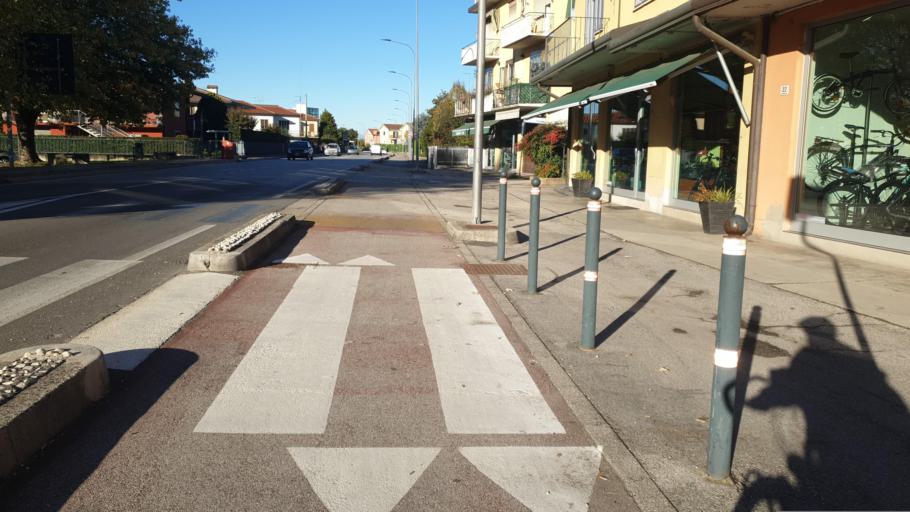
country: IT
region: Veneto
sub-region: Provincia di Venezia
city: Cazzago-Ex Polo
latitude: 45.4413
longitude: 12.0743
